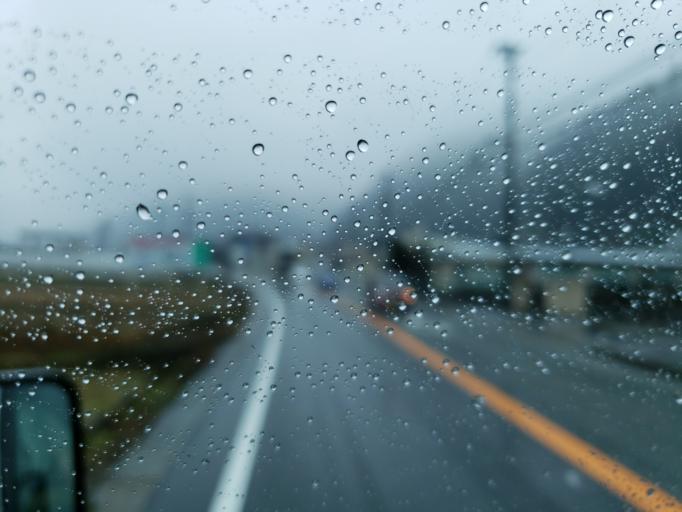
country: JP
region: Hyogo
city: Toyooka
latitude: 35.3872
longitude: 134.6896
